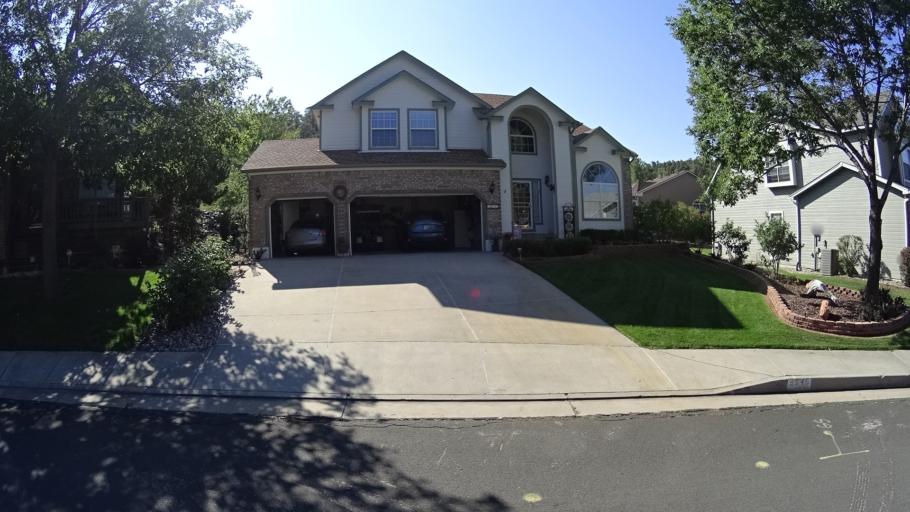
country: US
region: Colorado
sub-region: El Paso County
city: Colorado Springs
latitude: 38.8882
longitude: -104.7822
